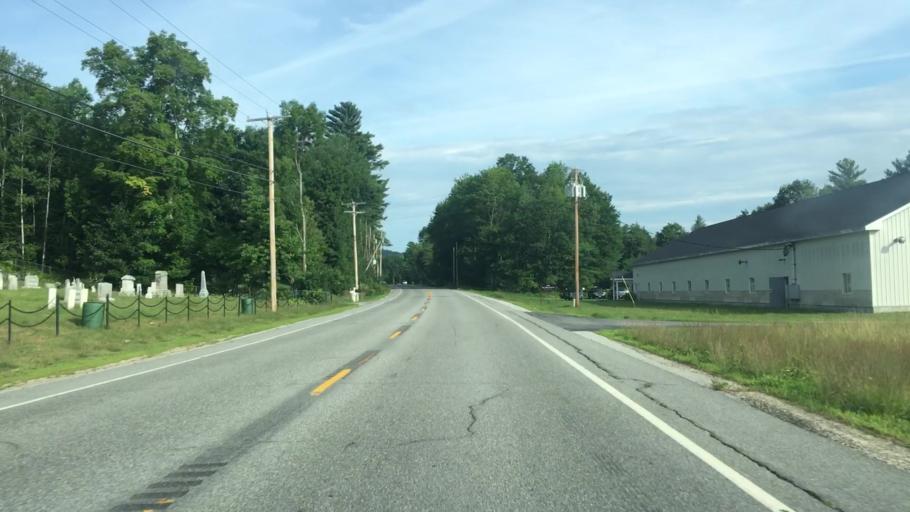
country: US
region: Maine
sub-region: York County
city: Limington
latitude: 43.7534
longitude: -70.6879
